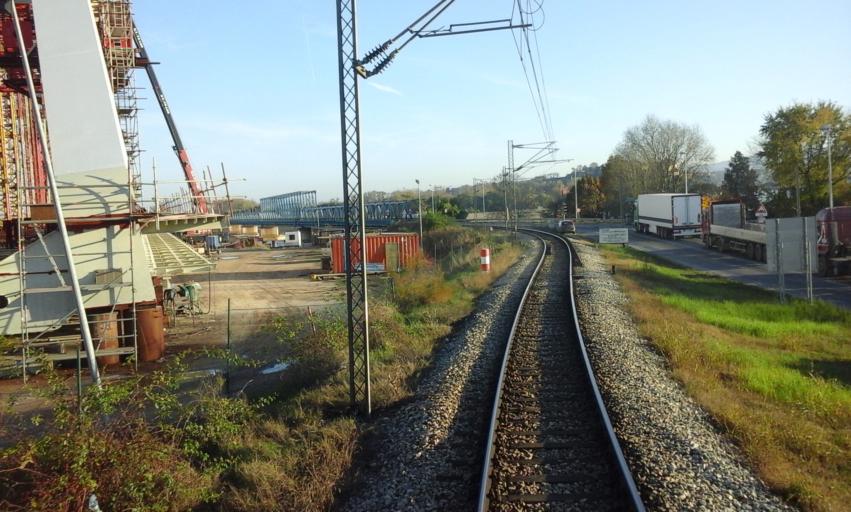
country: RS
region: Autonomna Pokrajina Vojvodina
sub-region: Juznobacki Okrug
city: Novi Sad
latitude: 45.2641
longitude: 19.8558
